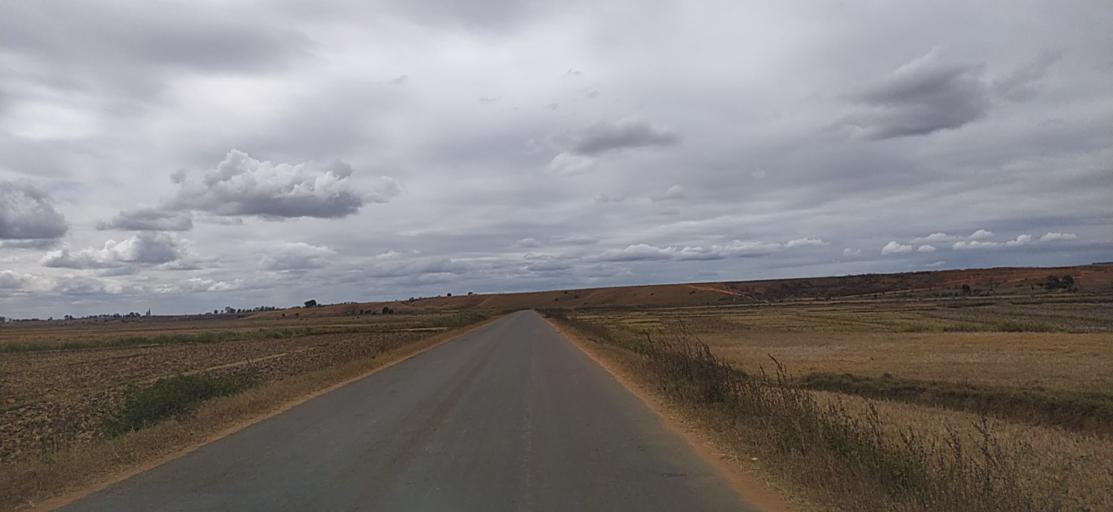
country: MG
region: Alaotra Mangoro
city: Ambatondrazaka
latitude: -17.9186
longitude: 48.2581
